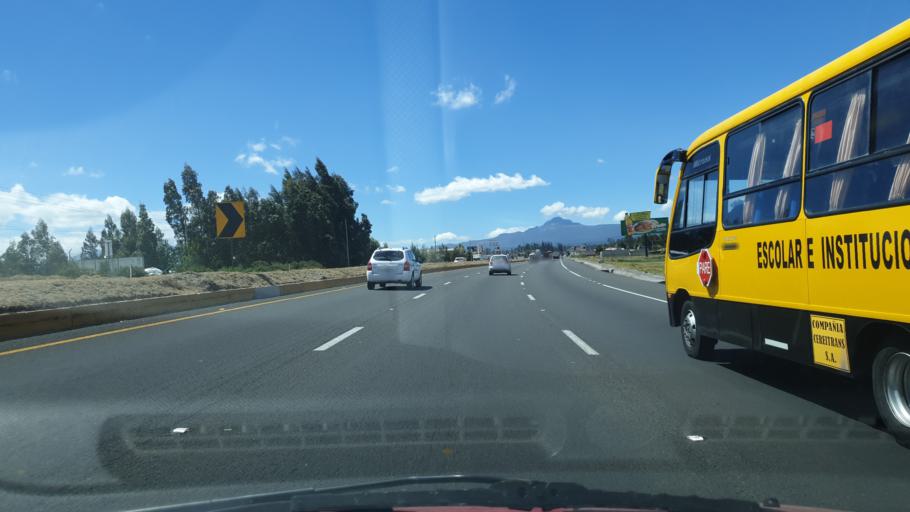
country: EC
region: Cotopaxi
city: Saquisili
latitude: -0.8119
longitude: -78.6249
